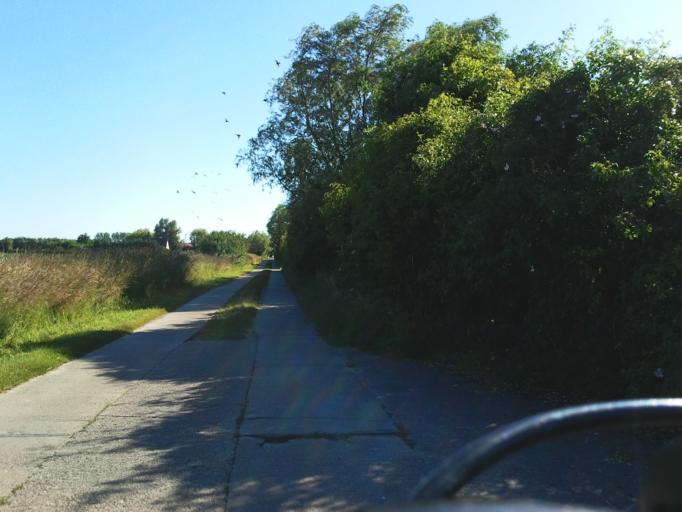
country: DE
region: Mecklenburg-Vorpommern
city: Monchhagen
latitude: 54.1641
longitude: 12.2010
